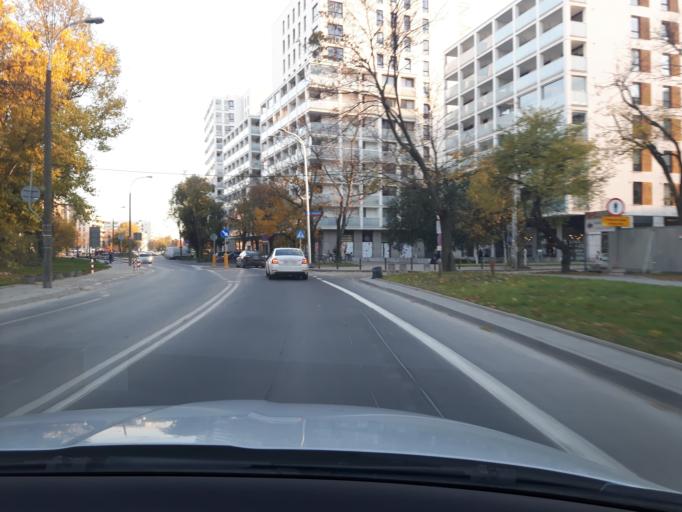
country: PL
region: Masovian Voivodeship
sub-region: Warszawa
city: Ochota
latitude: 52.2262
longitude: 20.9518
